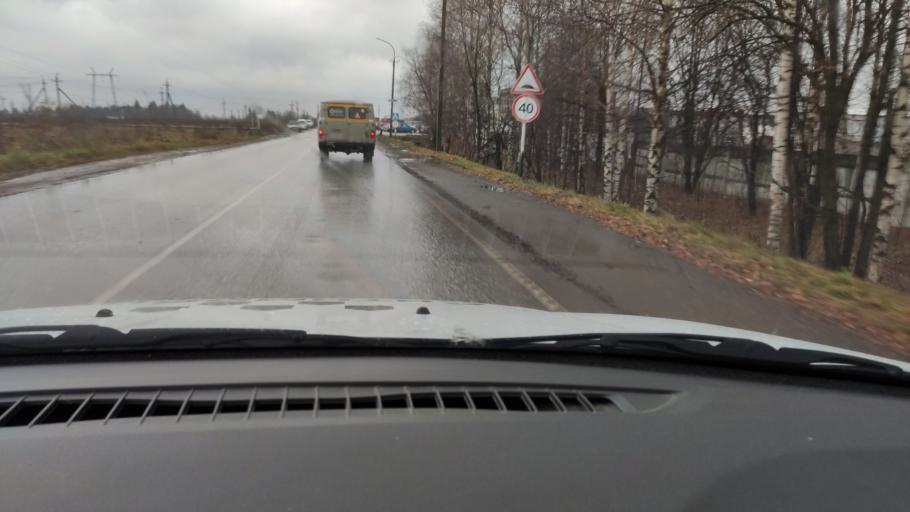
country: RU
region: Perm
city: Sylva
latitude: 58.0278
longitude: 56.7169
